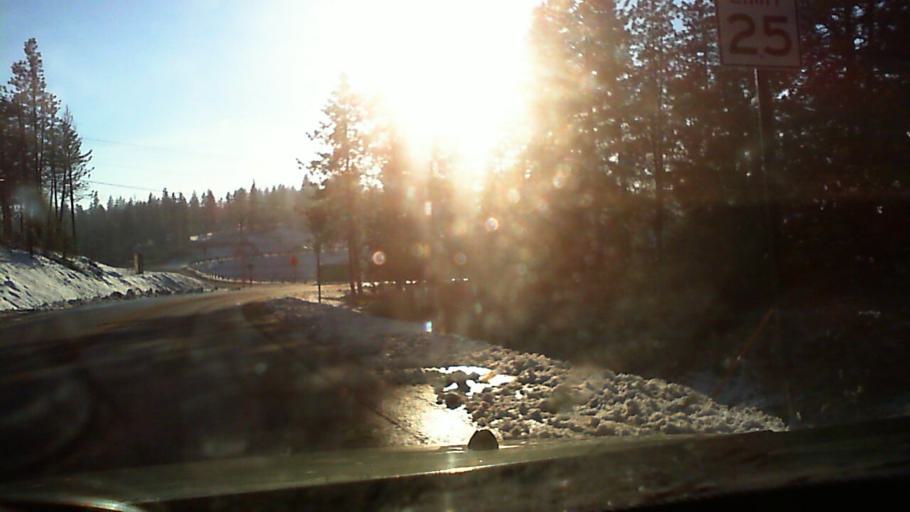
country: US
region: Washington
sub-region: Spokane County
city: Trentwood
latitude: 47.7229
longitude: -117.2128
